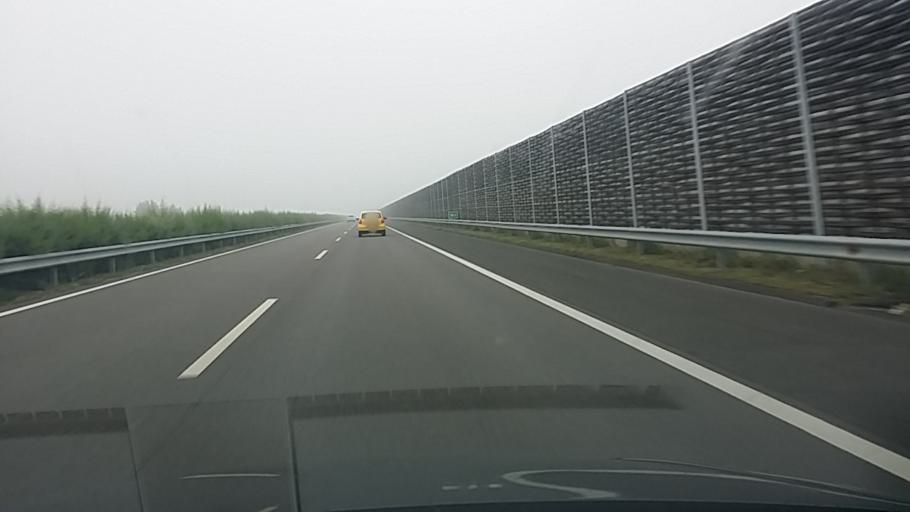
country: HU
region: Csongrad
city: Domaszek
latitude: 46.2701
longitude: 20.0396
